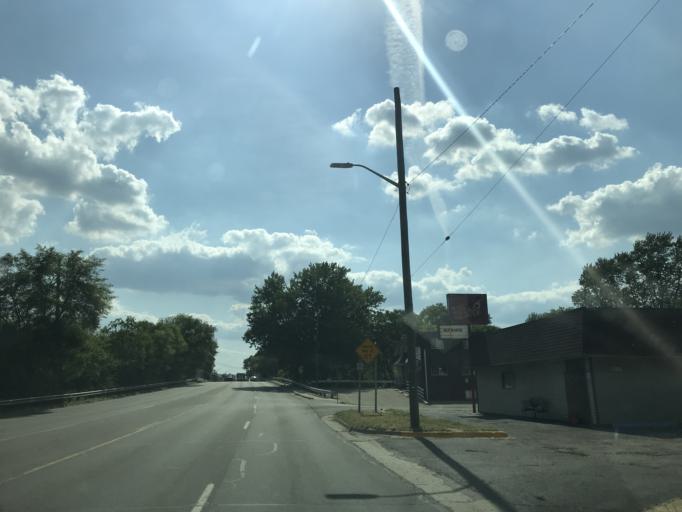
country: US
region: Michigan
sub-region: Washtenaw County
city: Ypsilanti
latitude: 42.2425
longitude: -83.5962
